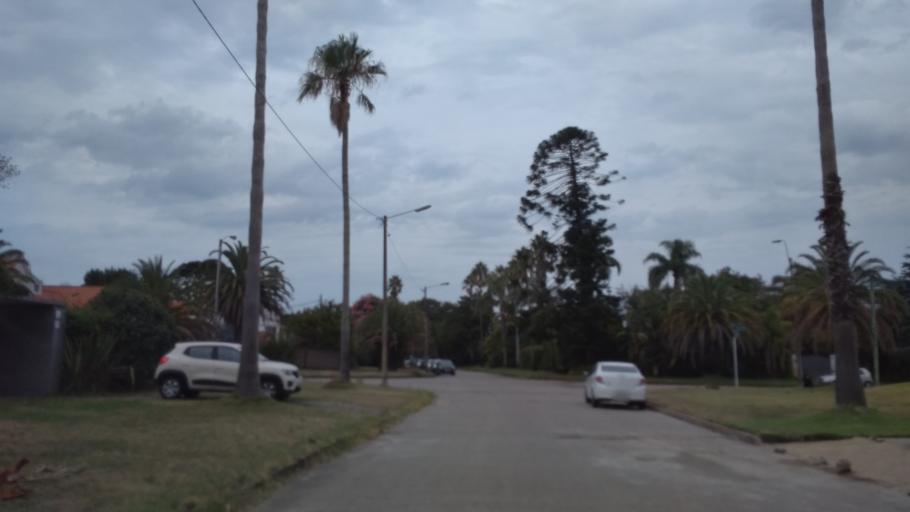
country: UY
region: Canelones
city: Barra de Carrasco
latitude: -34.8861
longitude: -56.0504
